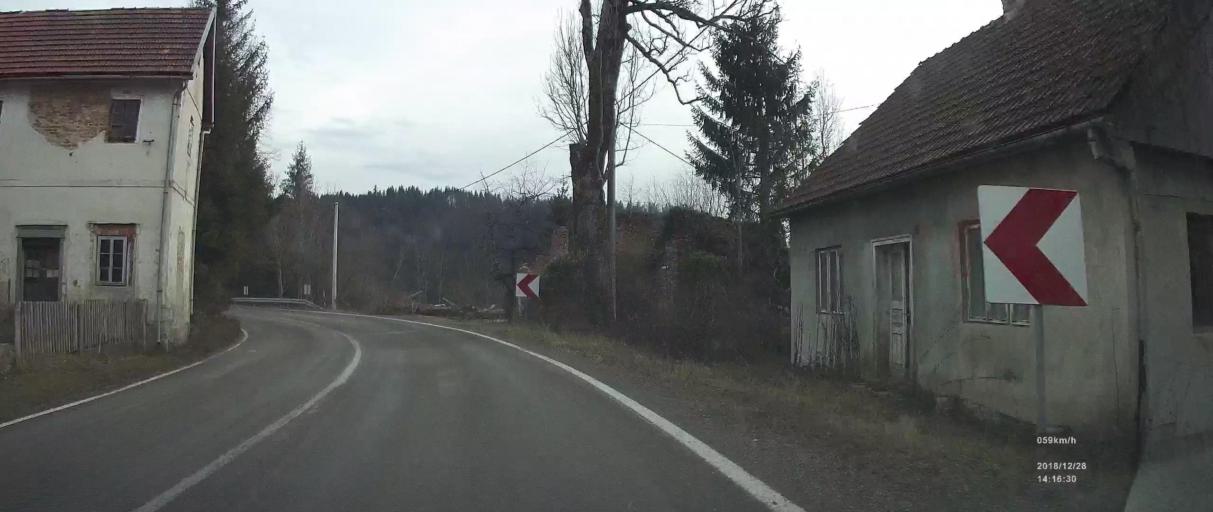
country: HR
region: Primorsko-Goranska
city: Vrbovsko
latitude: 45.4181
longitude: 15.0365
